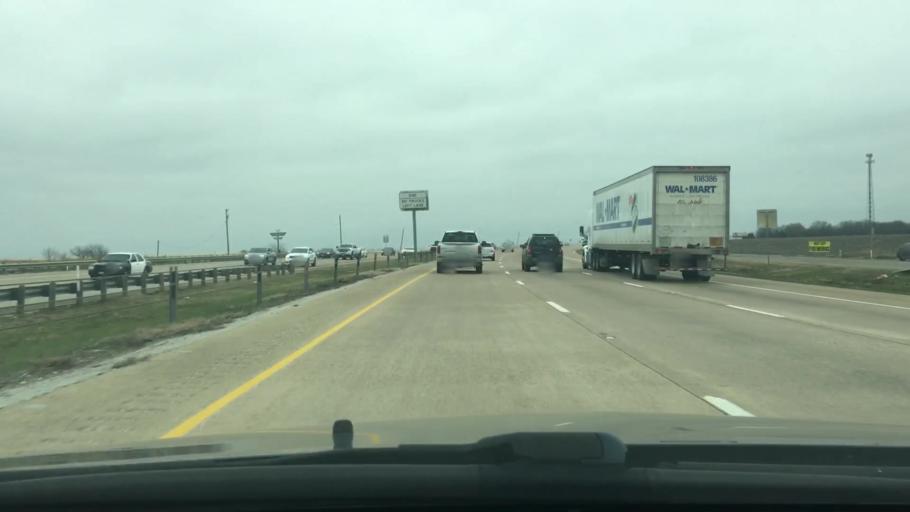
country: US
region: Texas
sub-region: Ellis County
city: Ennis
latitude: 32.2710
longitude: -96.5125
